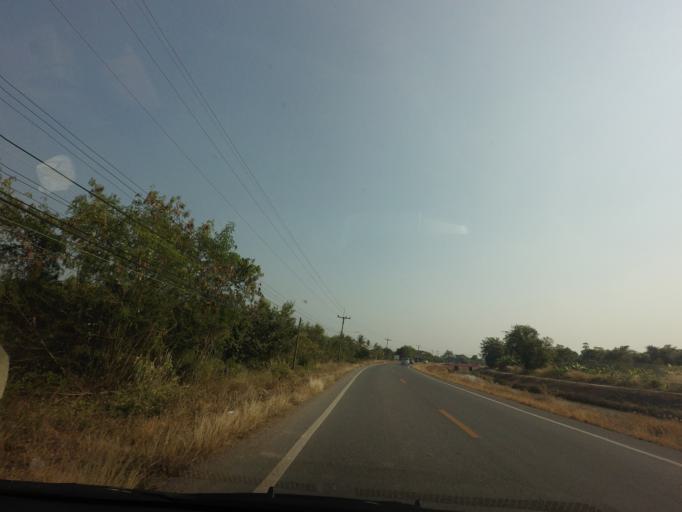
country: TH
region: Chachoengsao
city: Khlong Khuean
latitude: 13.8000
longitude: 101.1768
